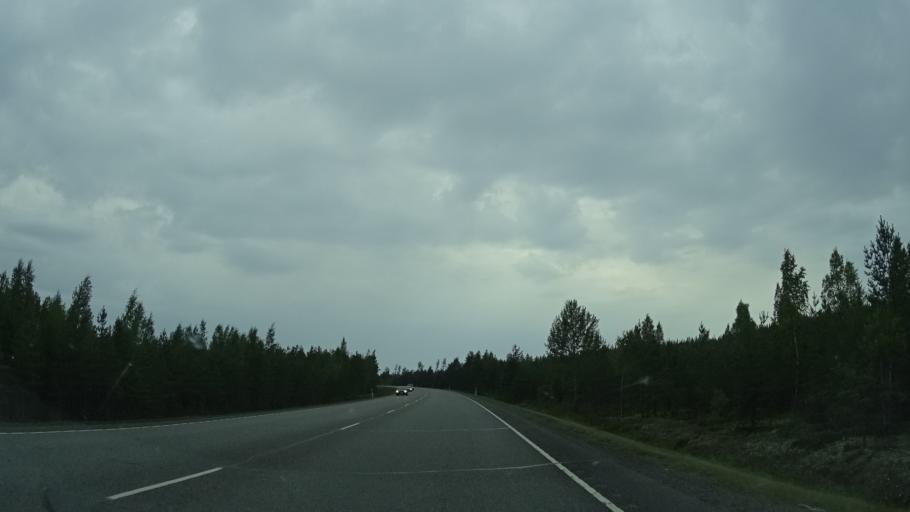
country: FI
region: Kymenlaakso
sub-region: Kouvola
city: Anjala
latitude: 60.9075
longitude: 27.0519
